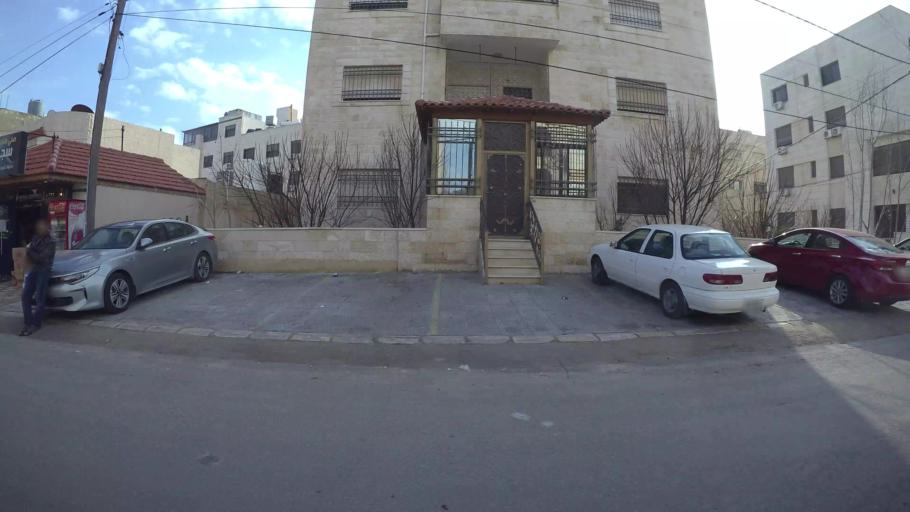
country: JO
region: Amman
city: Al Jubayhah
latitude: 31.9851
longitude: 35.8505
